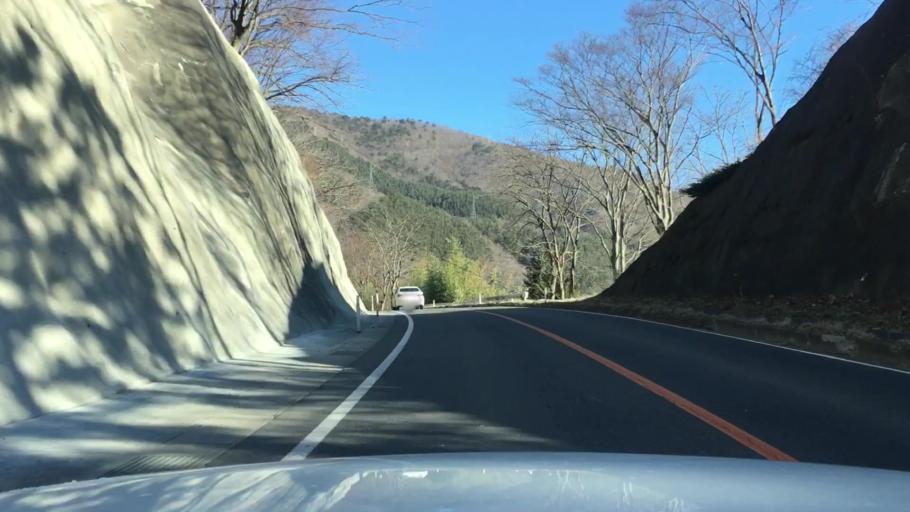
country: JP
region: Iwate
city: Miyako
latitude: 39.5952
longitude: 141.6763
